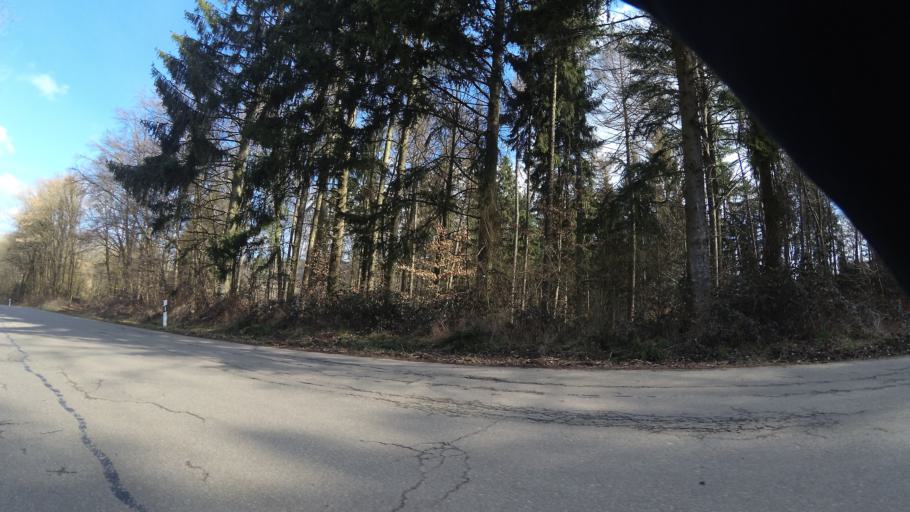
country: DE
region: Saarland
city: Rehlingen-Siersburg
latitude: 49.3942
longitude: 6.6586
